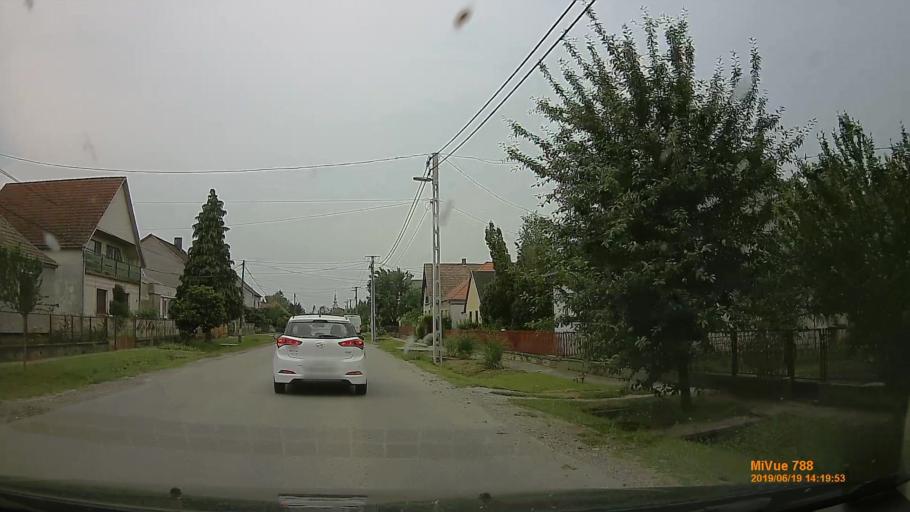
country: HU
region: Baranya
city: Szigetvar
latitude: 46.0287
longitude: 17.7790
